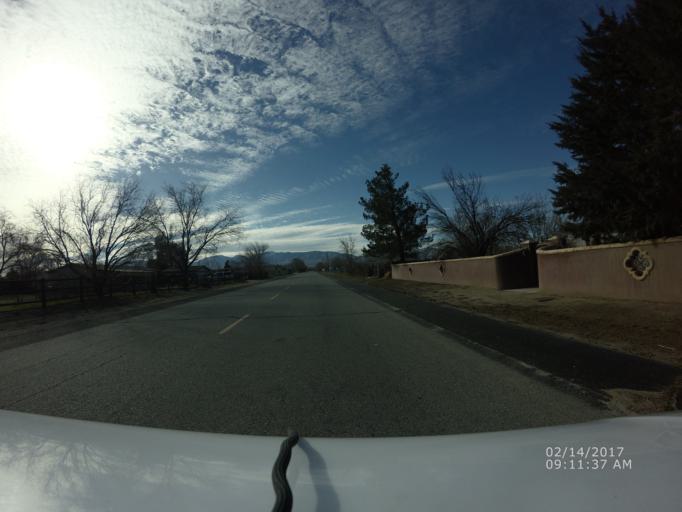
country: US
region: California
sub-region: Los Angeles County
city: Littlerock
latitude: 34.5632
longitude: -117.9431
